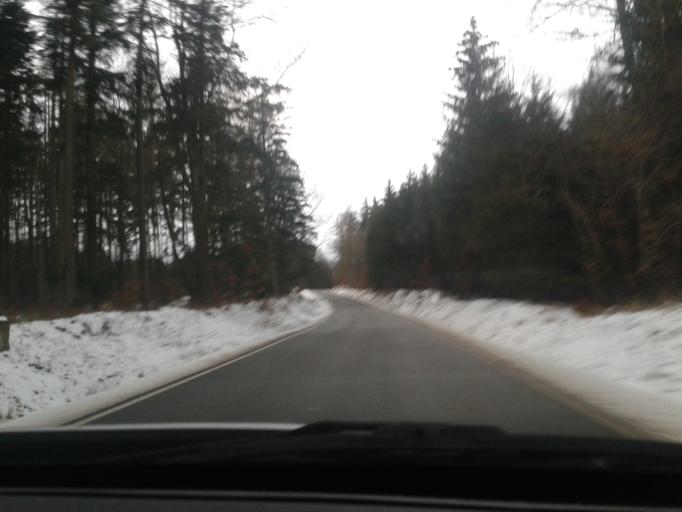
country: CZ
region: Olomoucky
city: Pteni
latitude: 49.5104
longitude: 16.9201
